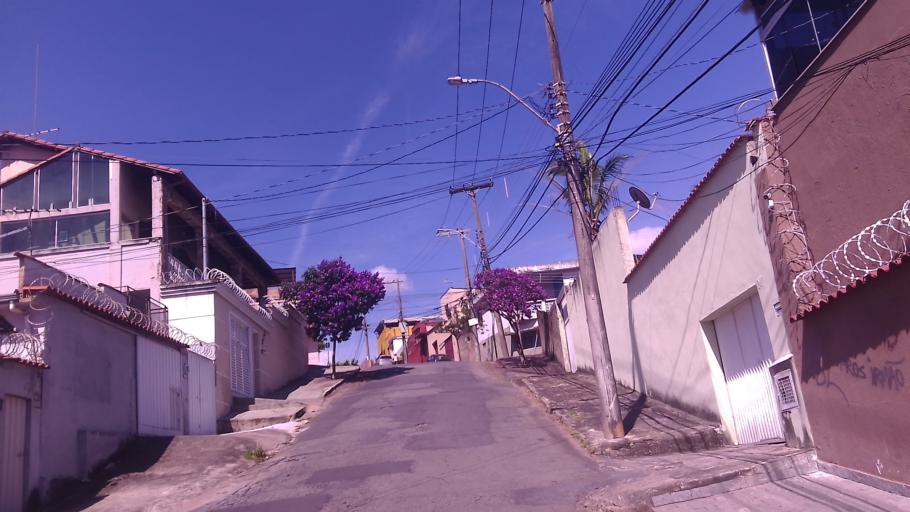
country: BR
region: Minas Gerais
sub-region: Contagem
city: Contagem
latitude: -19.9148
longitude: -44.0023
